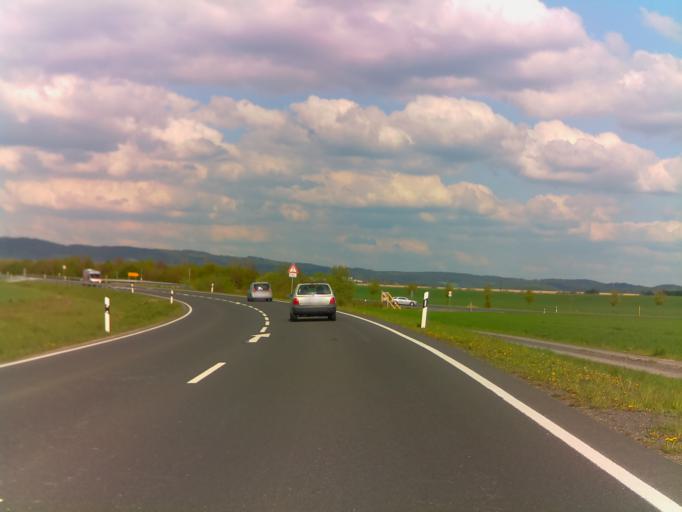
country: DE
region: Bavaria
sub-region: Upper Franconia
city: Ebersdorf
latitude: 50.3198
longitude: 11.1566
